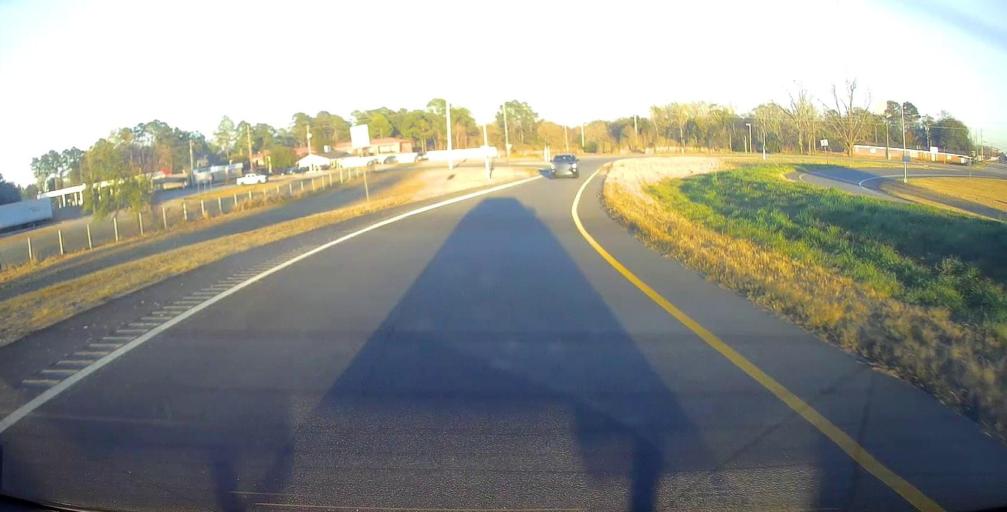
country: US
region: Georgia
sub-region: Dougherty County
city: Albany
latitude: 31.6178
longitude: -84.1774
